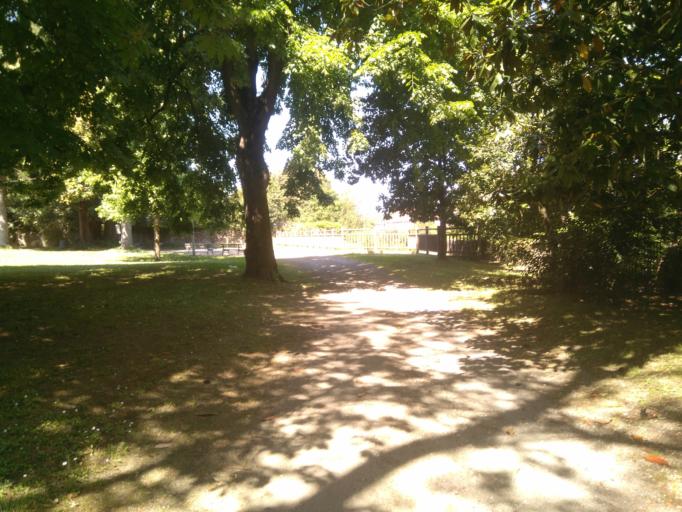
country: FR
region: Aquitaine
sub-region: Departement des Pyrenees-Atlantiques
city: Orthez
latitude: 43.4853
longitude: -0.7749
